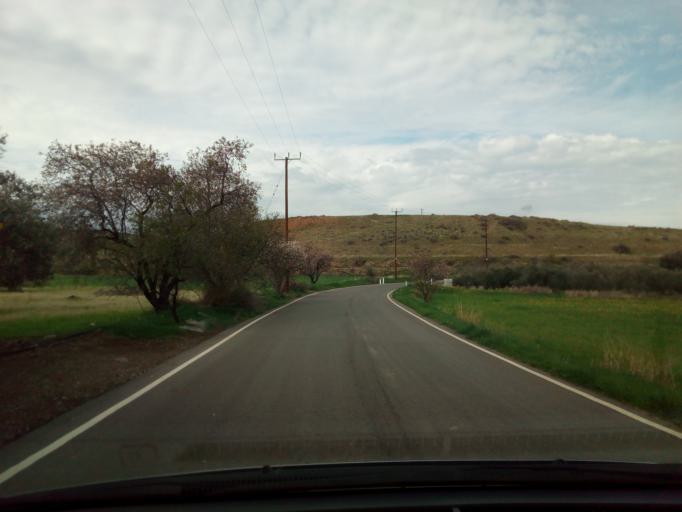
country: CY
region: Lefkosia
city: Astromeritis
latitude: 35.0847
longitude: 32.9947
